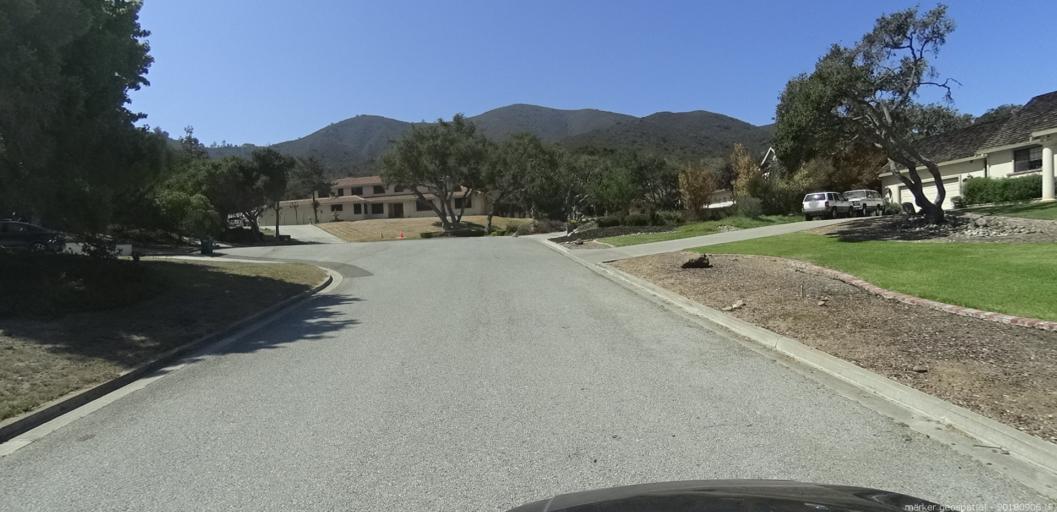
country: US
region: California
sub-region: Monterey County
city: Salinas
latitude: 36.5873
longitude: -121.6355
